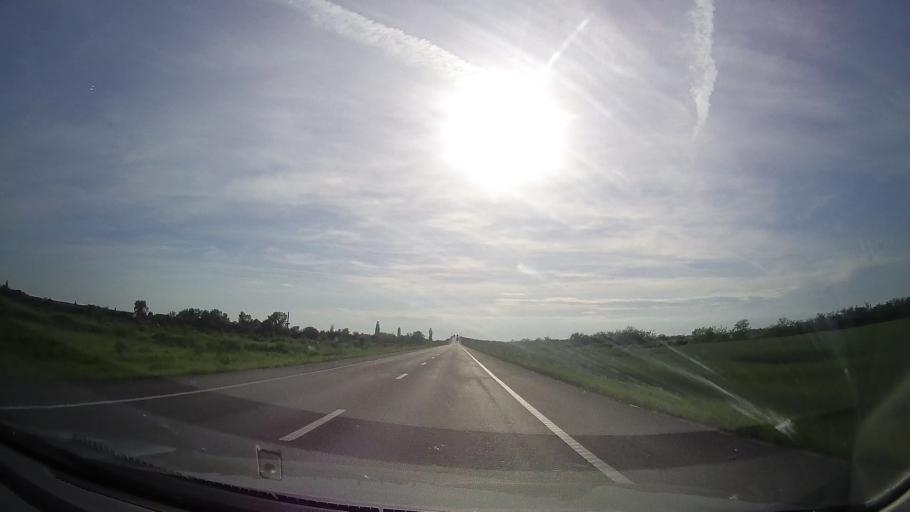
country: RO
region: Timis
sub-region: Municipiul Lugoj
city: Lugoj
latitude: 45.7217
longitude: 21.8868
